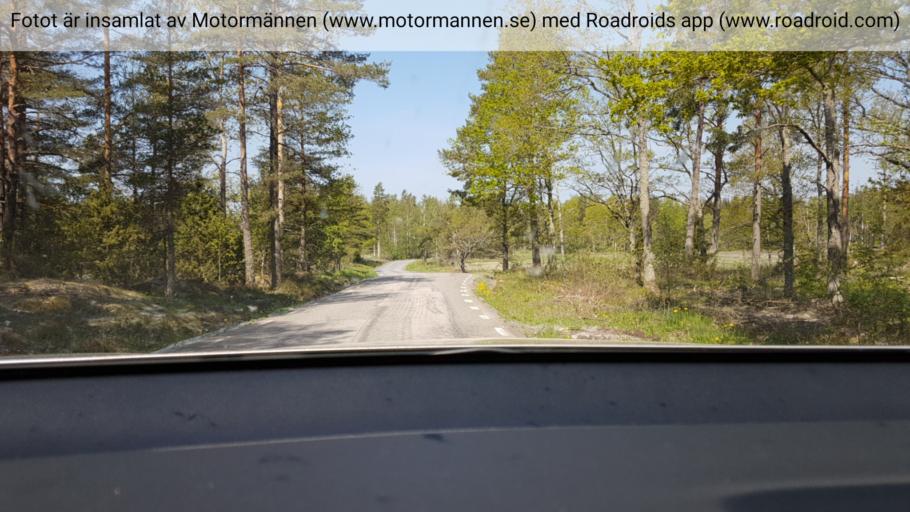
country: SE
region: Kalmar
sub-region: Vasterviks Kommun
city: Gamleby
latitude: 57.8724
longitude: 16.4558
